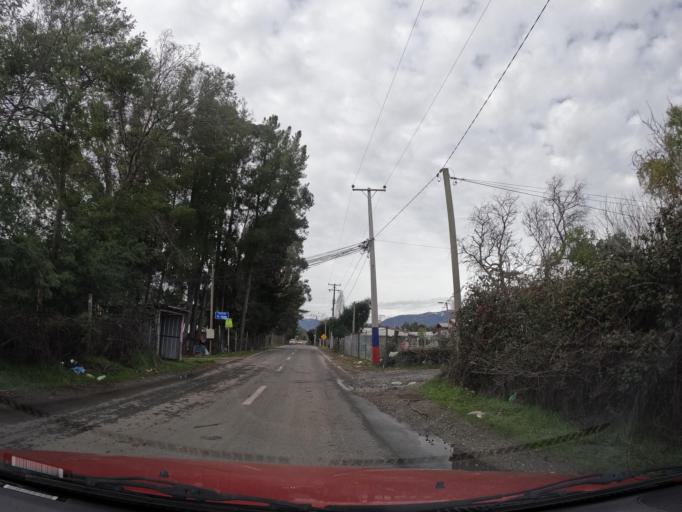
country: CL
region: Maule
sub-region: Provincia de Linares
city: Linares
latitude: -35.9230
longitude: -71.4064
